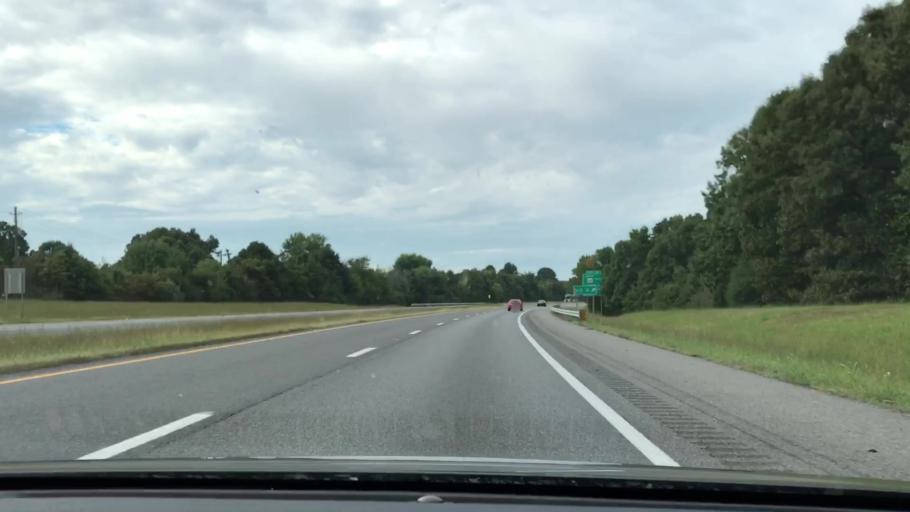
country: US
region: Kentucky
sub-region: Marshall County
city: Benton
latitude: 36.8538
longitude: -88.3702
